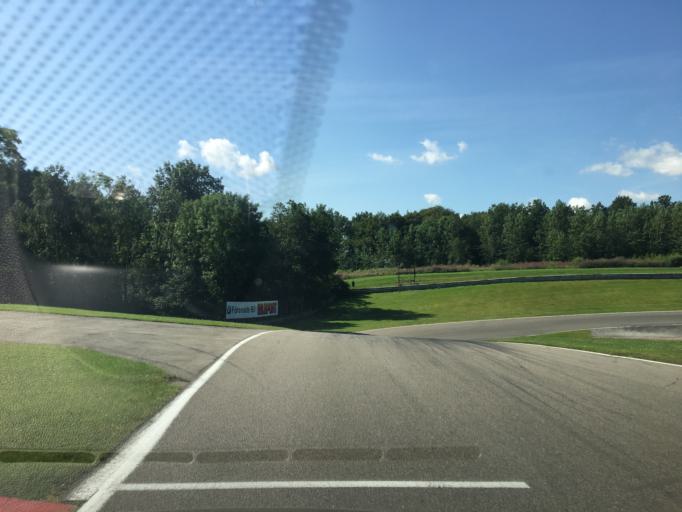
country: SE
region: Skane
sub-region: Svalovs Kommun
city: Kagerod
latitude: 55.9859
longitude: 13.1184
